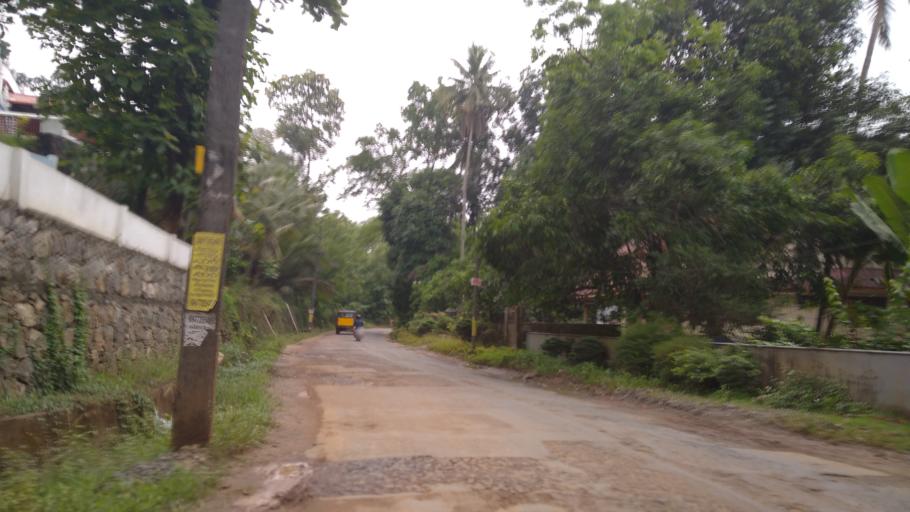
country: IN
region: Kerala
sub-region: Ernakulam
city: Perumpavur
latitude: 10.1215
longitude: 76.5533
